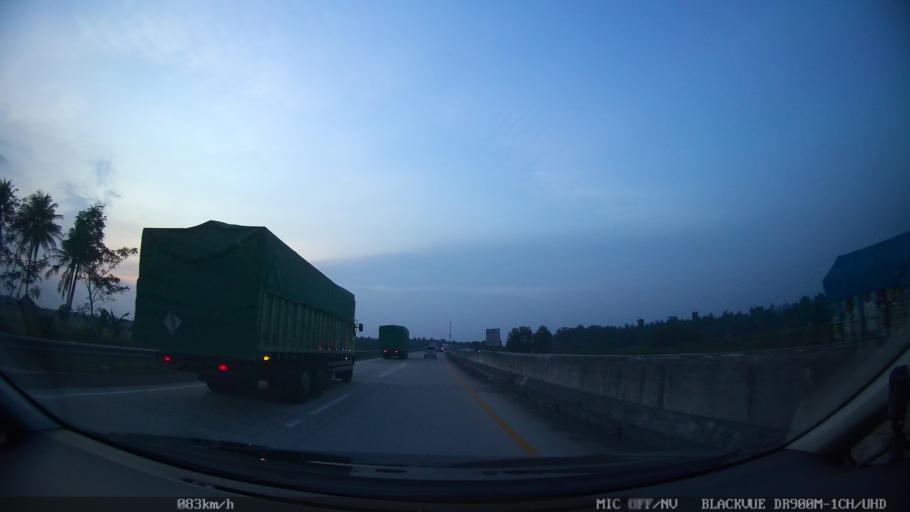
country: ID
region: Lampung
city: Kalianda
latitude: -5.6657
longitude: 105.5954
